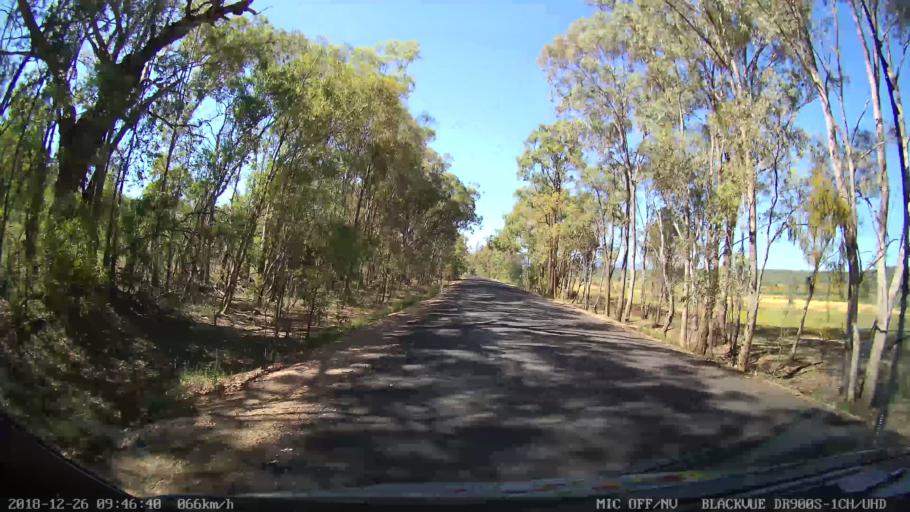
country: AU
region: New South Wales
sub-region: Mid-Western Regional
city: Kandos
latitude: -32.9719
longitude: 150.1049
